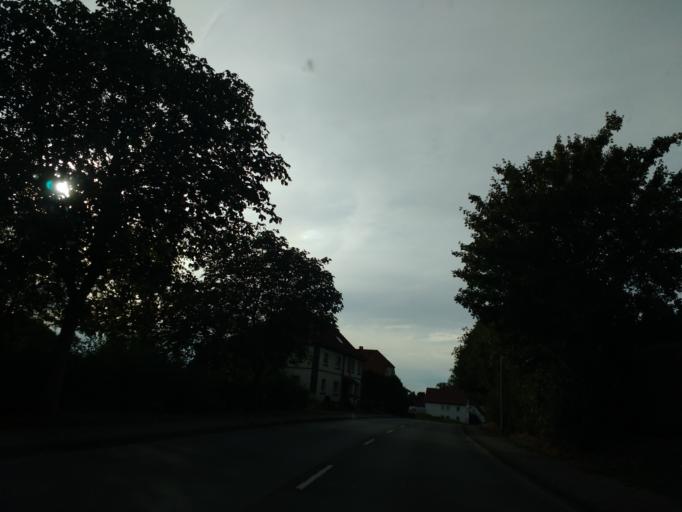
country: DE
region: North Rhine-Westphalia
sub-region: Regierungsbezirk Detmold
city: Blomberg
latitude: 51.9478
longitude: 9.0520
